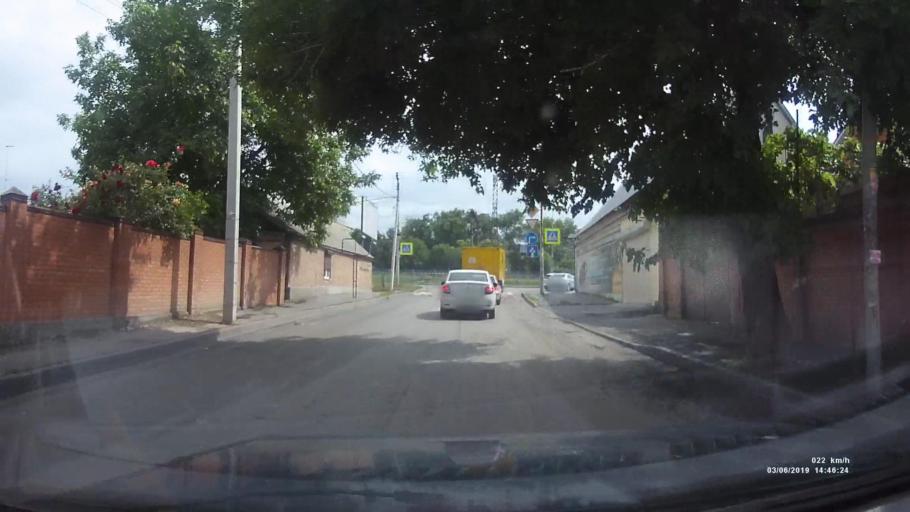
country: RU
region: Rostov
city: Rostov-na-Donu
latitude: 47.2449
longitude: 39.7241
